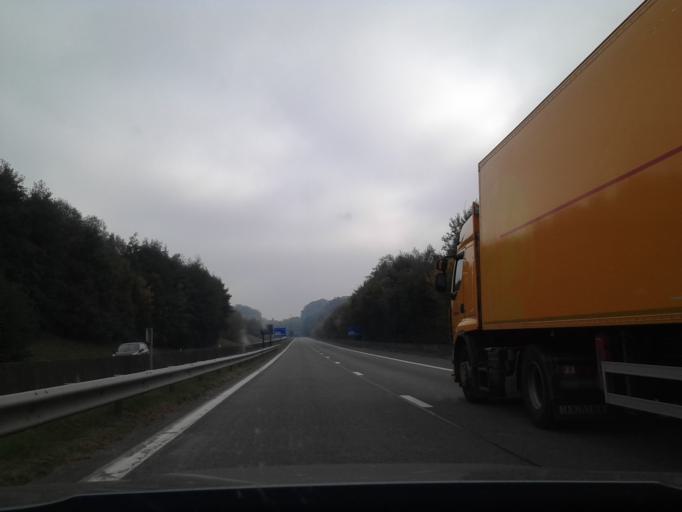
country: BE
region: Wallonia
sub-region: Province du Hainaut
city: Frasnes-lez-Buissenal
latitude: 50.6572
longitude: 3.6548
